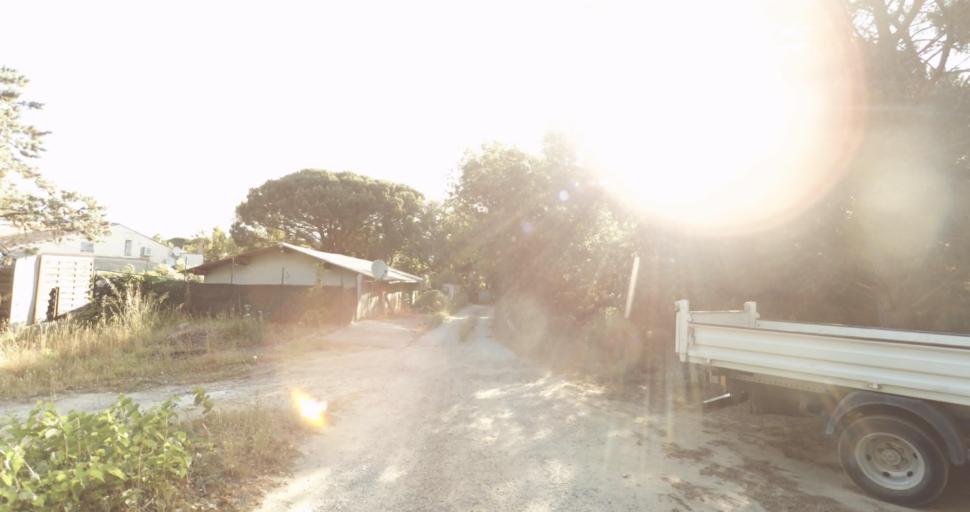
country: FR
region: Provence-Alpes-Cote d'Azur
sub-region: Departement du Var
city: Saint-Tropez
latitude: 43.2558
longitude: 6.6346
